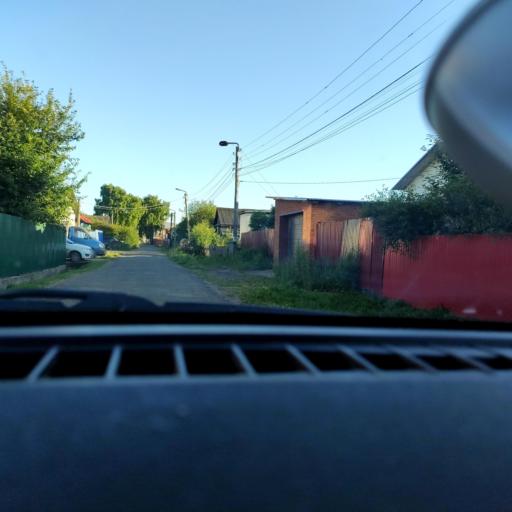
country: RU
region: Perm
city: Froly
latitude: 57.8897
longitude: 56.2553
